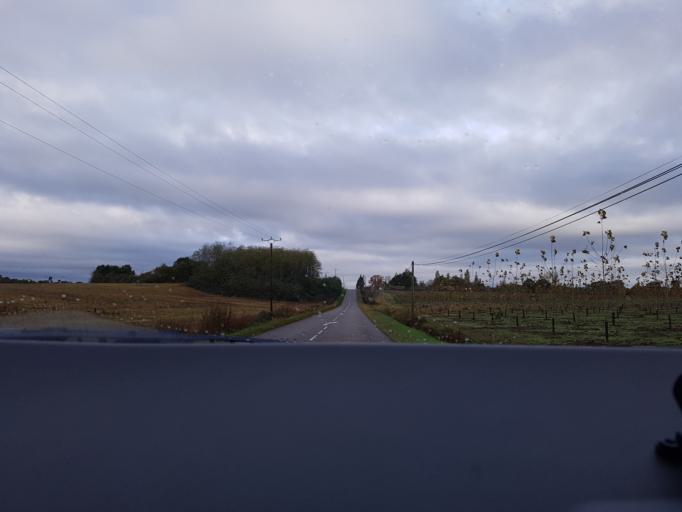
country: FR
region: Midi-Pyrenees
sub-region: Departement du Gers
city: Cazaubon
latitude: 43.9481
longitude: -0.1515
